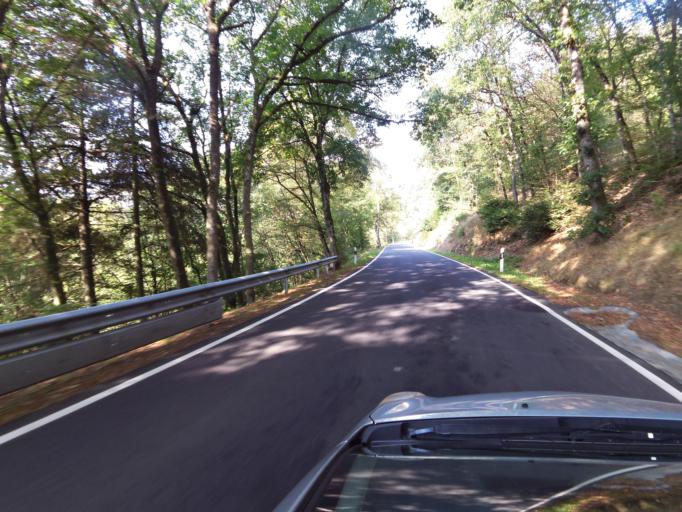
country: LU
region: Diekirch
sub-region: Canton de Wiltz
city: Goesdorf
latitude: 49.9091
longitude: 5.9728
